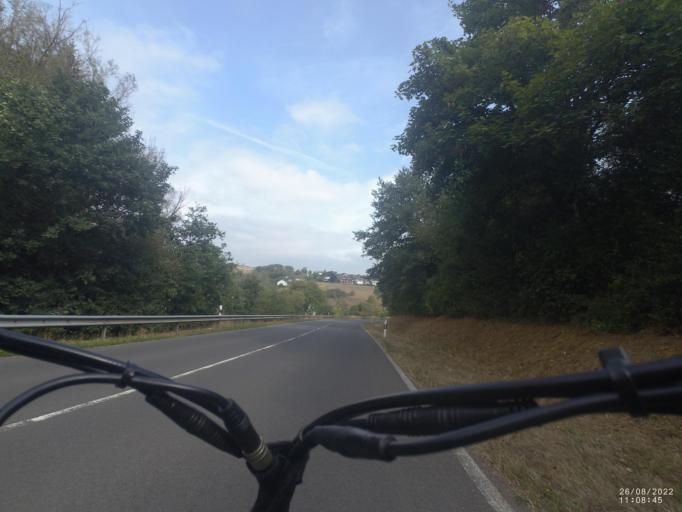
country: DE
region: Rheinland-Pfalz
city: Birresborn
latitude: 50.2122
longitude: 6.6315
